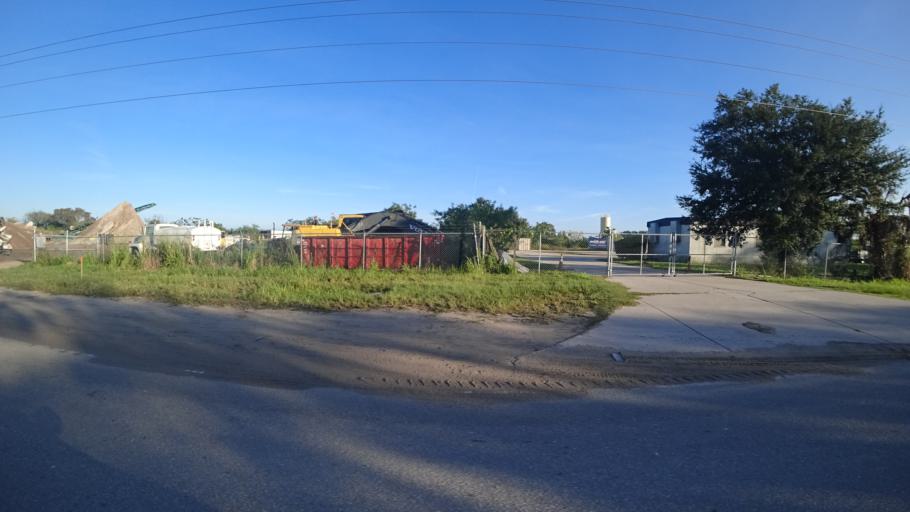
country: US
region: Florida
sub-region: Manatee County
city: Ellenton
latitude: 27.5291
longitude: -82.5338
